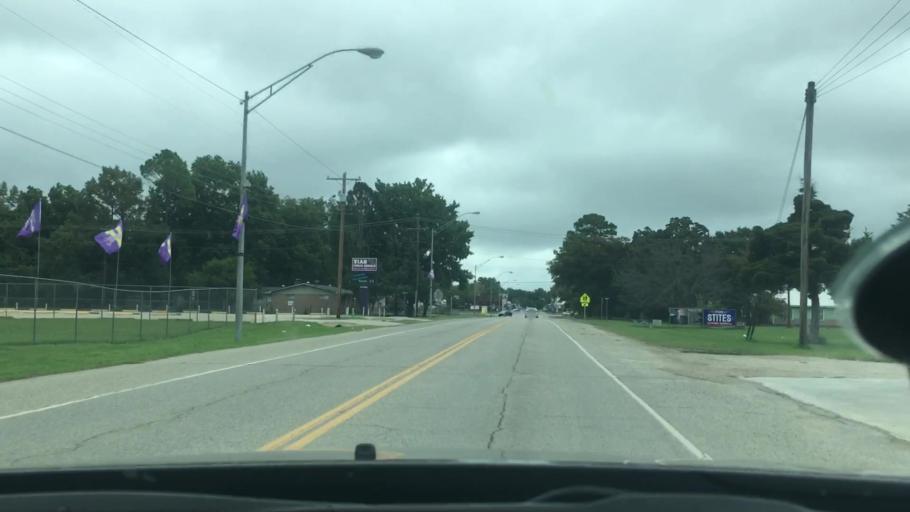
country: US
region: Oklahoma
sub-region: Sequoyah County
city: Vian
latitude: 35.4940
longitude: -94.9710
